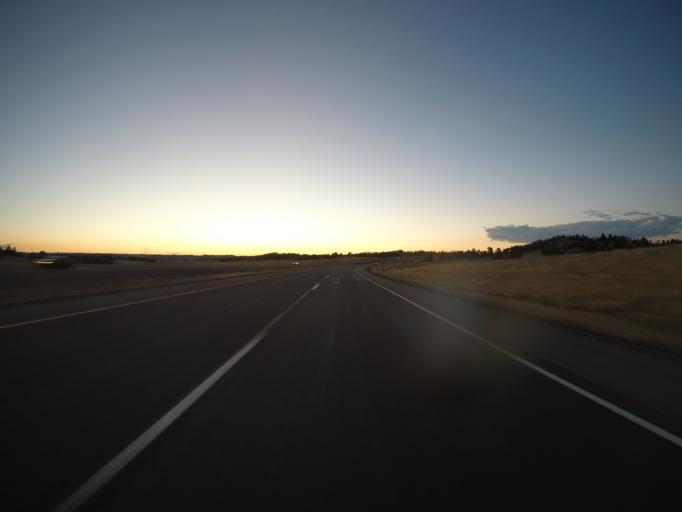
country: US
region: Wyoming
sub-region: Albany County
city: Laramie
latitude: 41.0050
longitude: -105.4169
